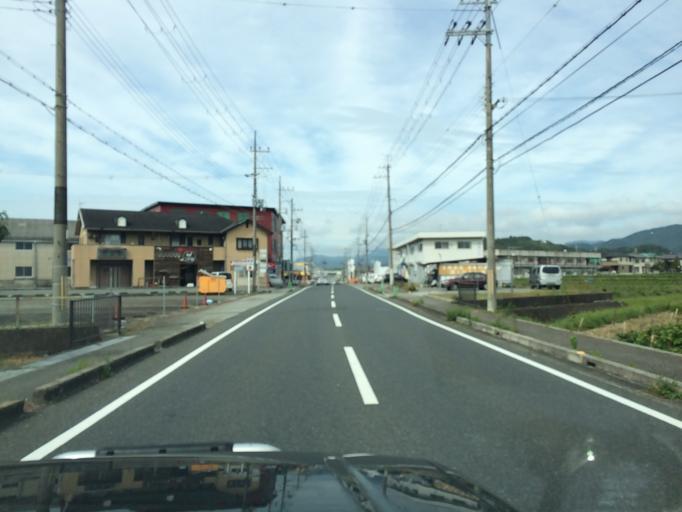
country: JP
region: Hyogo
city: Sasayama
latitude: 35.0699
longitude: 135.2124
